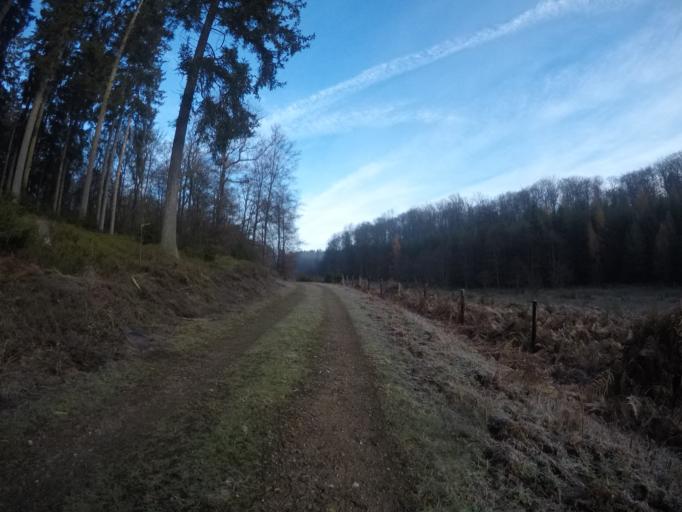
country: BE
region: Wallonia
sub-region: Province du Luxembourg
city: Habay-la-Vieille
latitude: 49.7597
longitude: 5.6602
